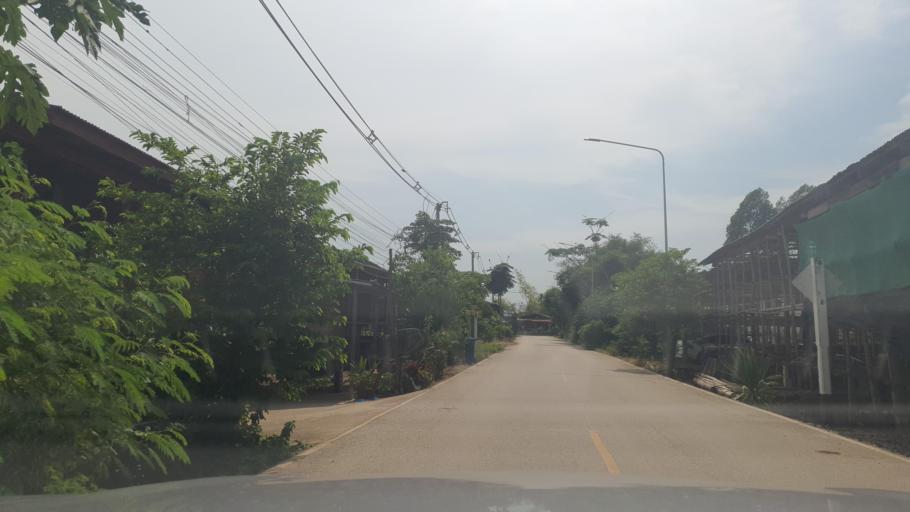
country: TH
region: Sukhothai
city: Si Samrong
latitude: 17.1415
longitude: 99.8310
